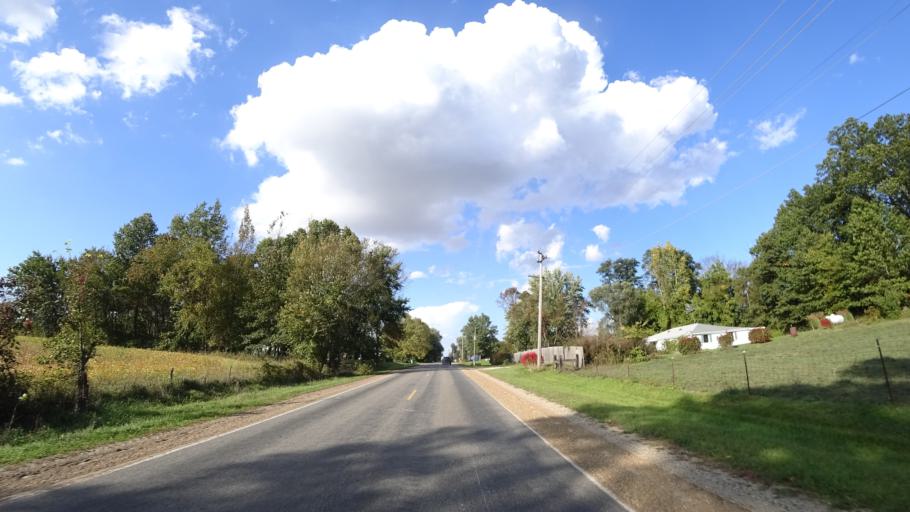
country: US
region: Michigan
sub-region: Saint Joseph County
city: Centreville
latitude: 41.9501
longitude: -85.5278
